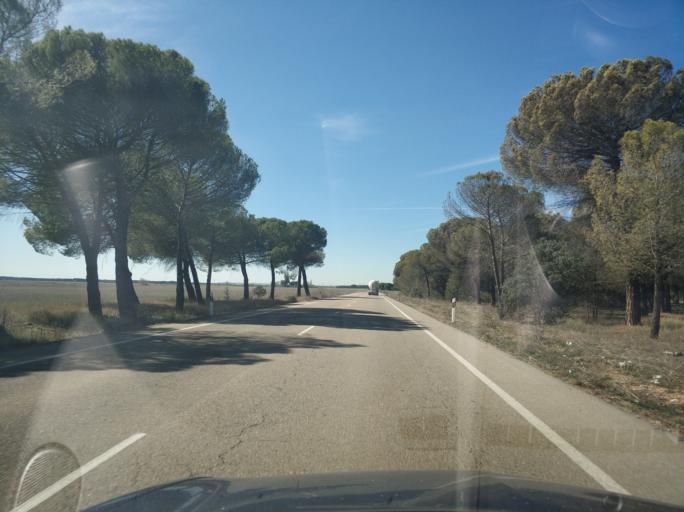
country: ES
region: Castille and Leon
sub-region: Provincia de Valladolid
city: Aldeamayor de San Martin
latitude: 41.5583
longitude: -4.6270
